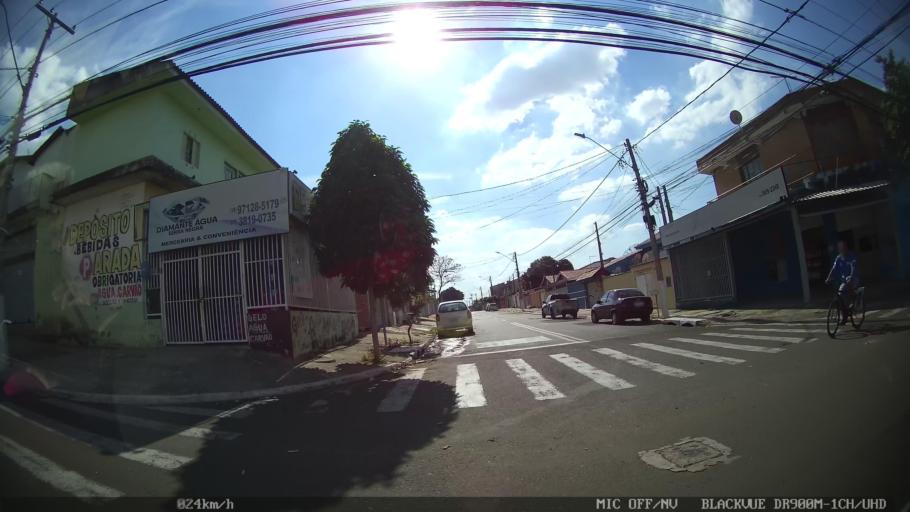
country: BR
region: Sao Paulo
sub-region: Hortolandia
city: Hortolandia
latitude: -22.9013
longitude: -47.2458
